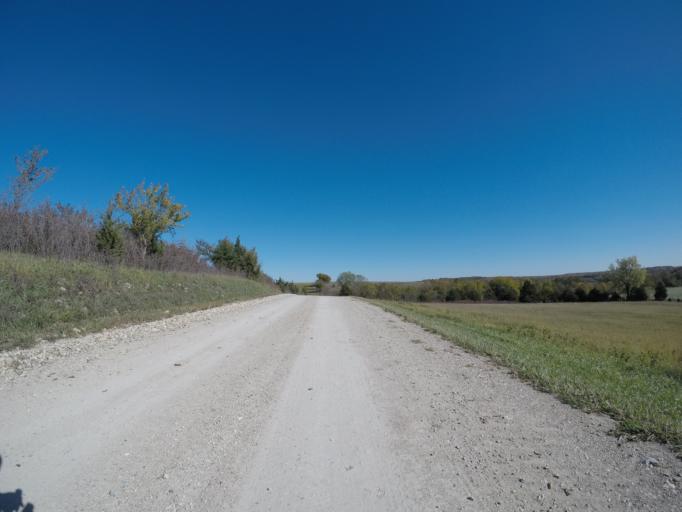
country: US
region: Kansas
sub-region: Wabaunsee County
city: Alma
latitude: 38.9420
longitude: -96.4295
